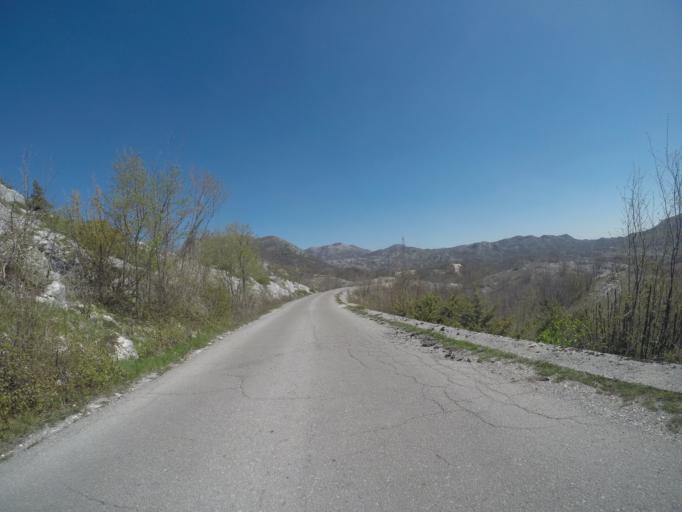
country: ME
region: Cetinje
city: Cetinje
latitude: 42.4398
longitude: 18.8725
